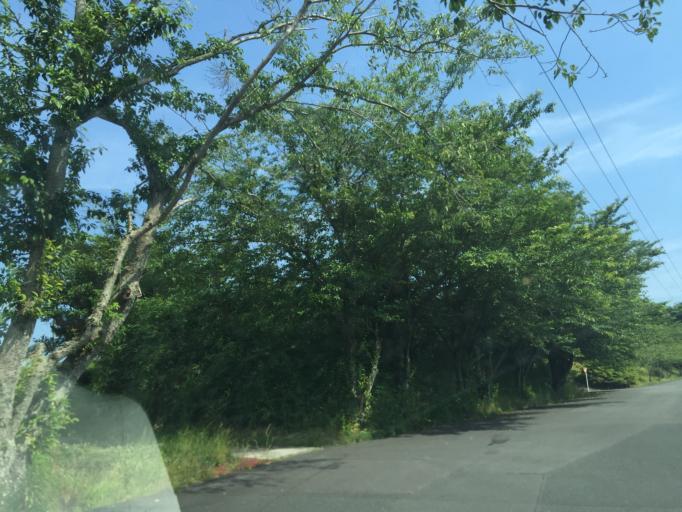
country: JP
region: Shizuoka
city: Kakegawa
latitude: 34.7550
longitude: 138.0017
